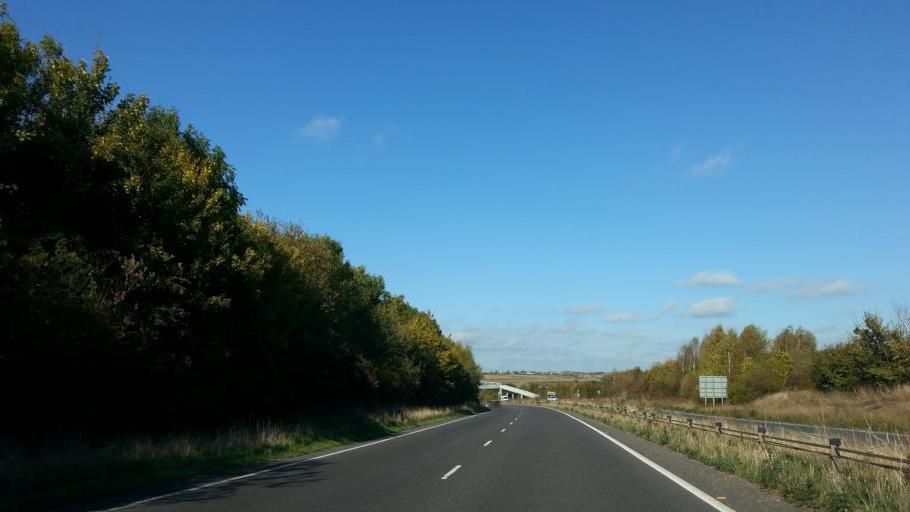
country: GB
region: England
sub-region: Northamptonshire
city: Higham Ferrers
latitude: 52.3153
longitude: -0.5879
